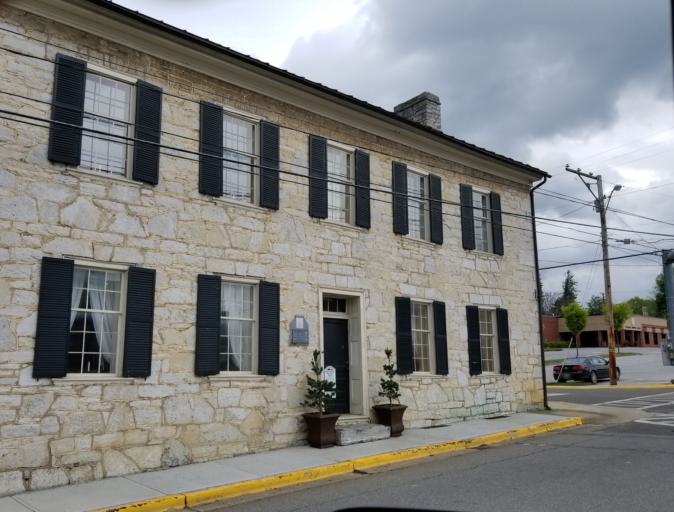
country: US
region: Virginia
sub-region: Wythe County
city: Wytheville
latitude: 36.9504
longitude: -81.0844
